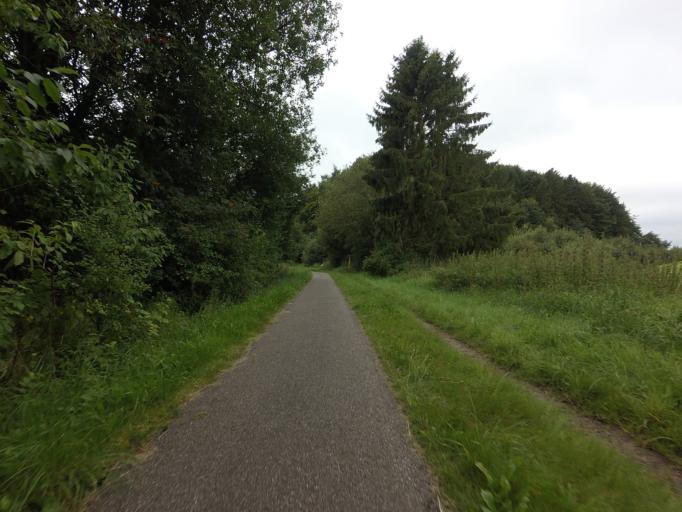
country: DK
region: Central Jutland
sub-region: Silkeborg Kommune
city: Virklund
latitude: 56.1084
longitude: 9.5601
